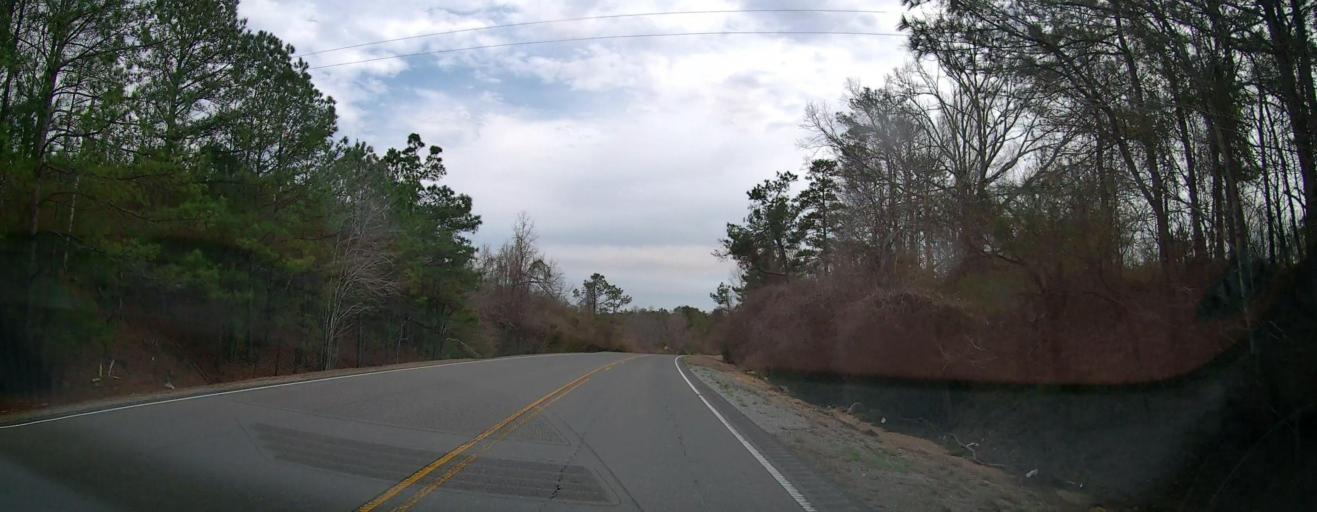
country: US
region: Alabama
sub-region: Marion County
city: Guin
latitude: 34.0281
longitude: -87.9417
